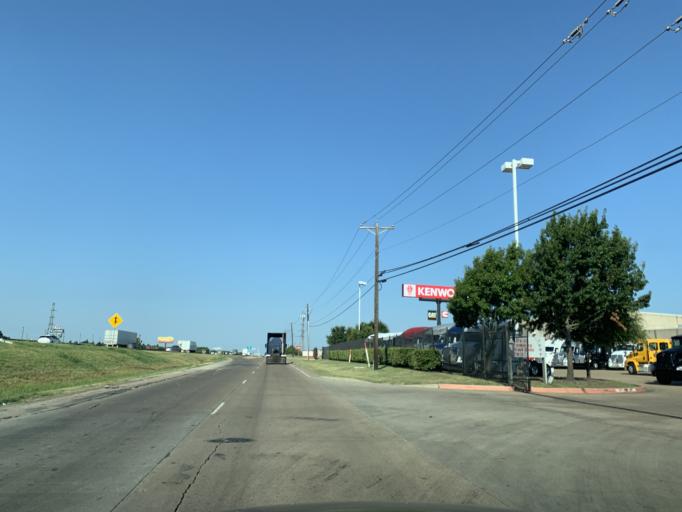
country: US
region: Texas
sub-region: Dallas County
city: Hutchins
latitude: 32.6540
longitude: -96.7586
